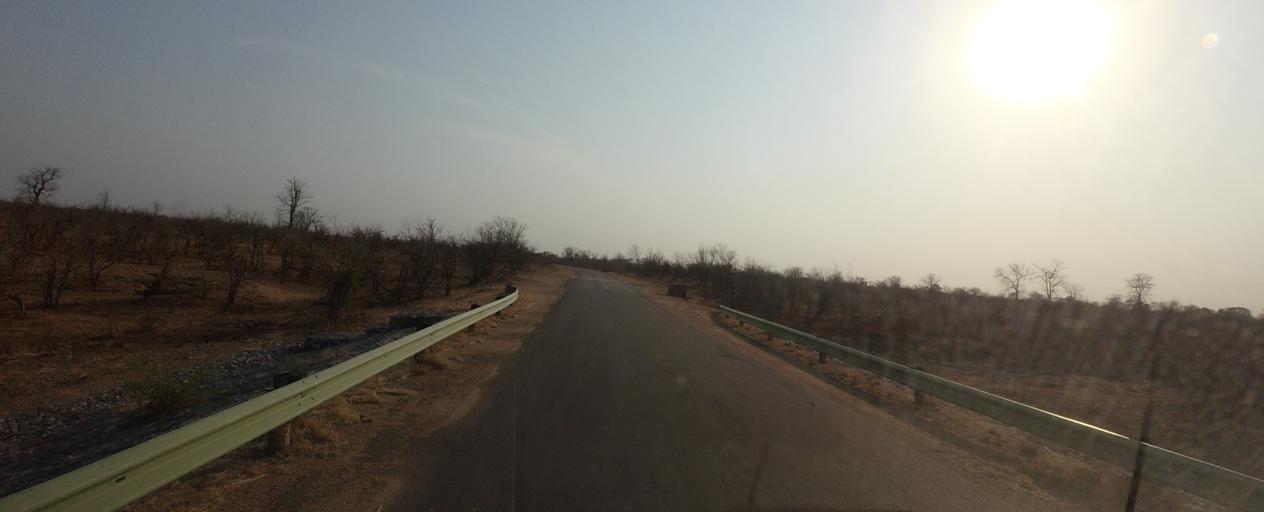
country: ZA
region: Limpopo
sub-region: Mopani District Municipality
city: Giyani
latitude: -23.0930
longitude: 31.4192
